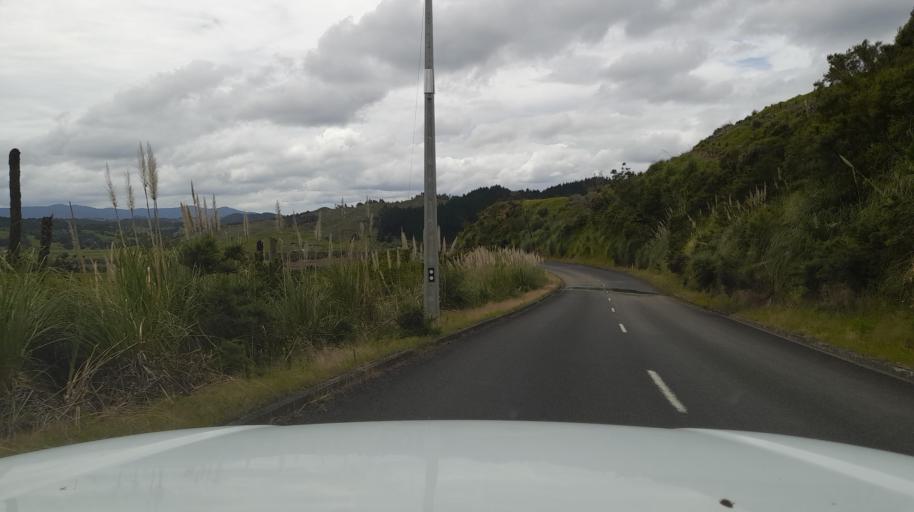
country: NZ
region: Northland
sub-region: Far North District
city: Kaitaia
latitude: -35.3685
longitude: 173.4318
